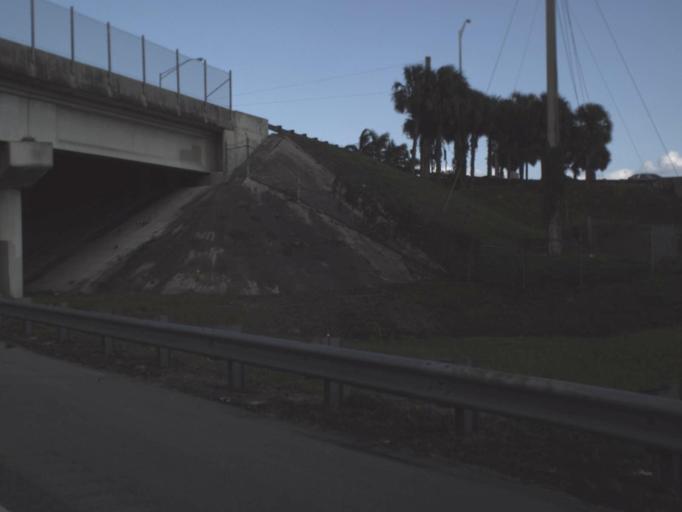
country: US
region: Florida
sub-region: Broward County
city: Coconut Creek
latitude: 26.2312
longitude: -80.1776
